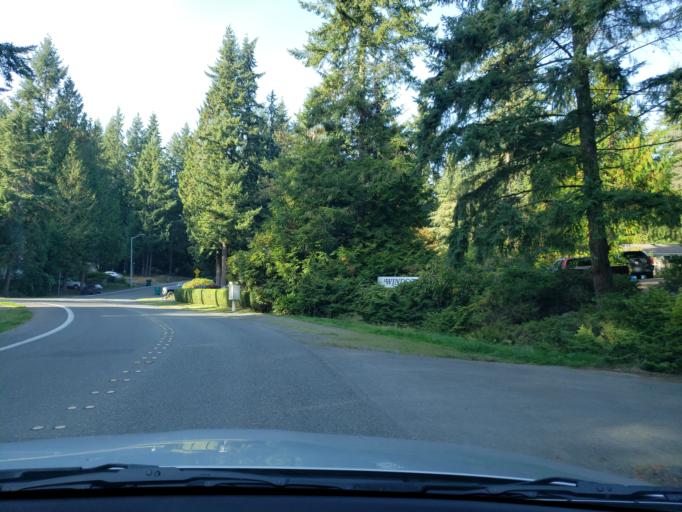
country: US
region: Washington
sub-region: Snohomish County
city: Meadowdale
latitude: 47.8688
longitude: -122.3146
